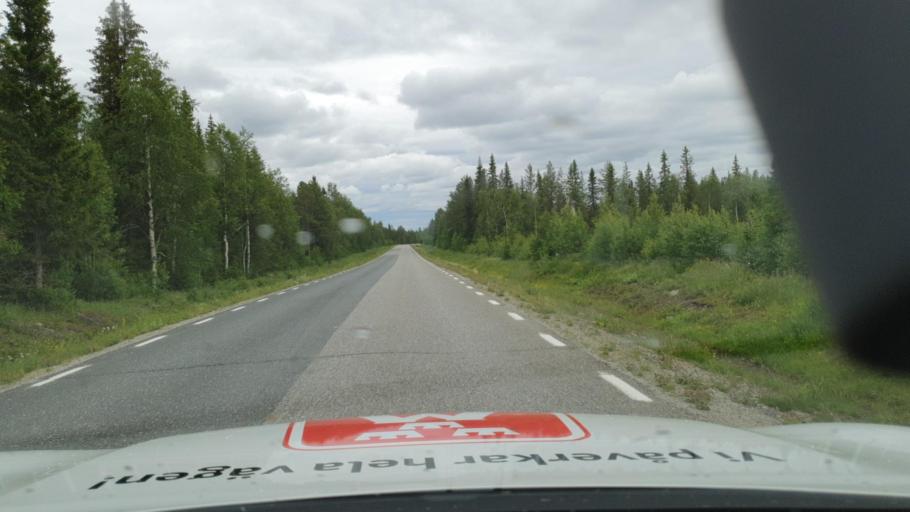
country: SE
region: Vaesterbotten
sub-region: Lycksele Kommun
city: Soderfors
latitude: 64.2764
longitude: 18.1984
